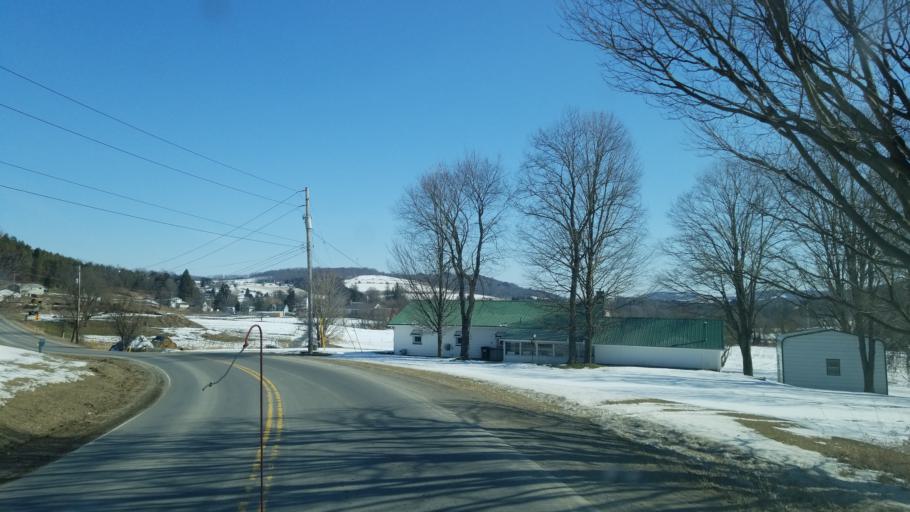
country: US
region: Pennsylvania
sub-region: Tioga County
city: Elkland
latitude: 42.0766
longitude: -77.4193
